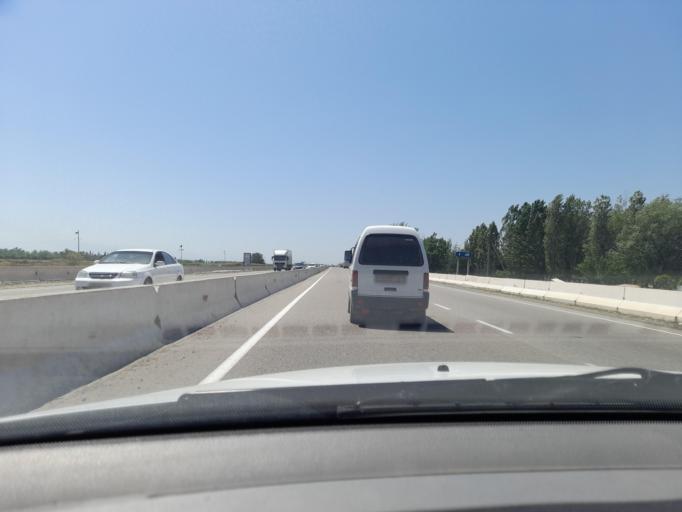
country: UZ
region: Jizzax
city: Dustlik
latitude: 40.3638
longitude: 68.1464
